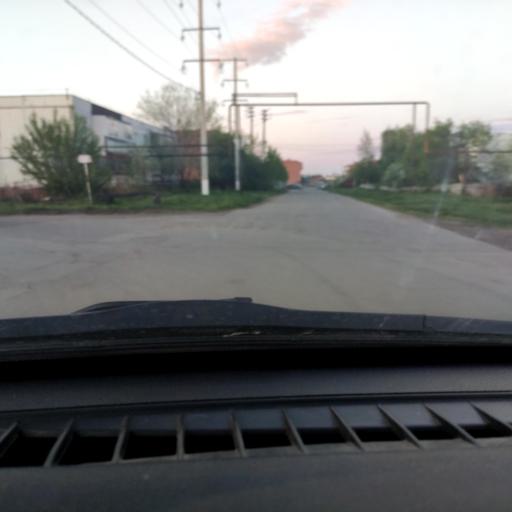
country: RU
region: Samara
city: Podstepki
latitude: 53.5168
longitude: 49.1124
